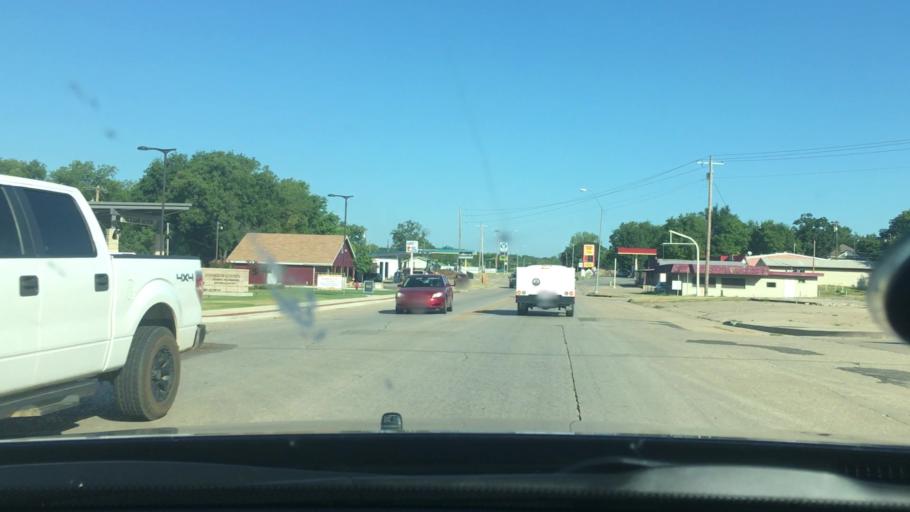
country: US
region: Oklahoma
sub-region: Johnston County
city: Tishomingo
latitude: 34.2368
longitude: -96.6809
